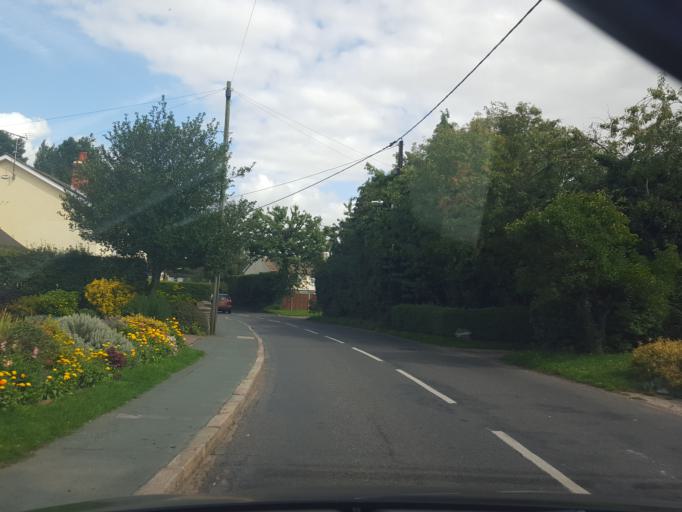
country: GB
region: England
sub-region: Essex
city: Mistley
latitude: 51.9254
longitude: 1.1077
